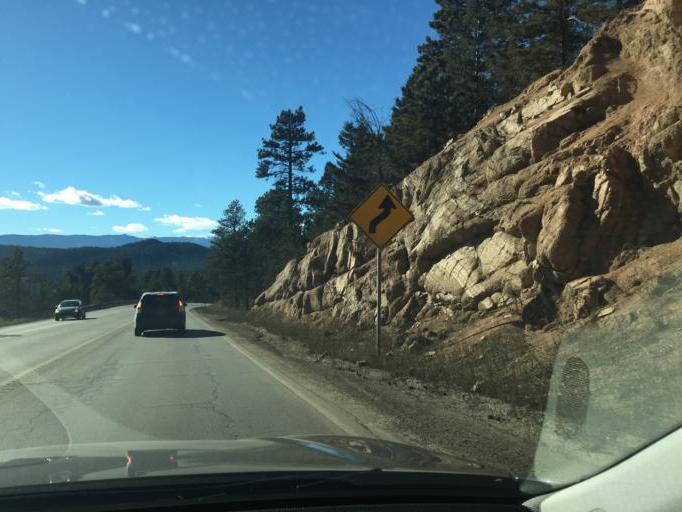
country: US
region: Colorado
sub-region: Jefferson County
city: Evergreen
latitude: 39.4893
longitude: -105.3551
